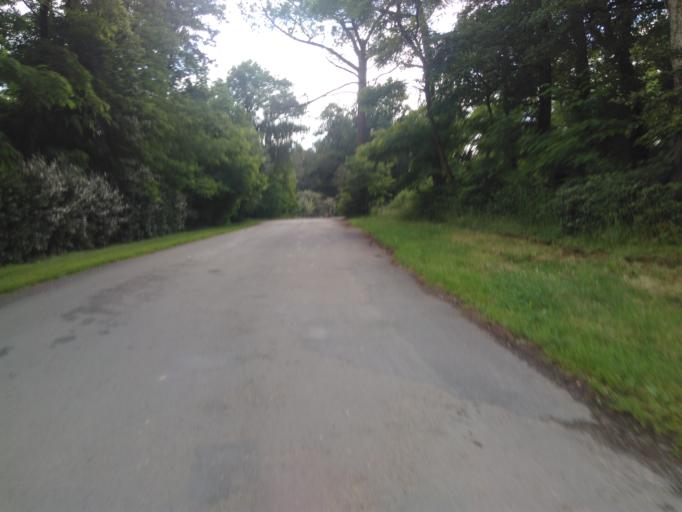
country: FR
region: Pays de la Loire
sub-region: Departement de la Vendee
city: La Ferriere
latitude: 46.7050
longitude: -1.3183
